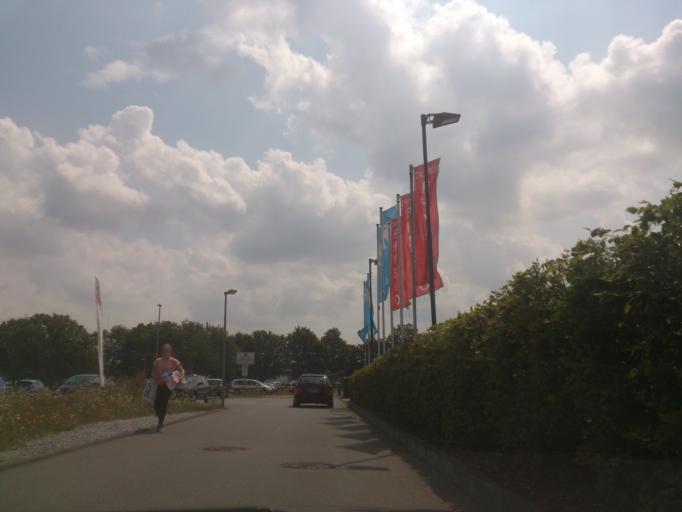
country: DE
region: North Rhine-Westphalia
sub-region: Regierungsbezirk Detmold
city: Paderborn
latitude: 51.7057
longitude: 8.7654
